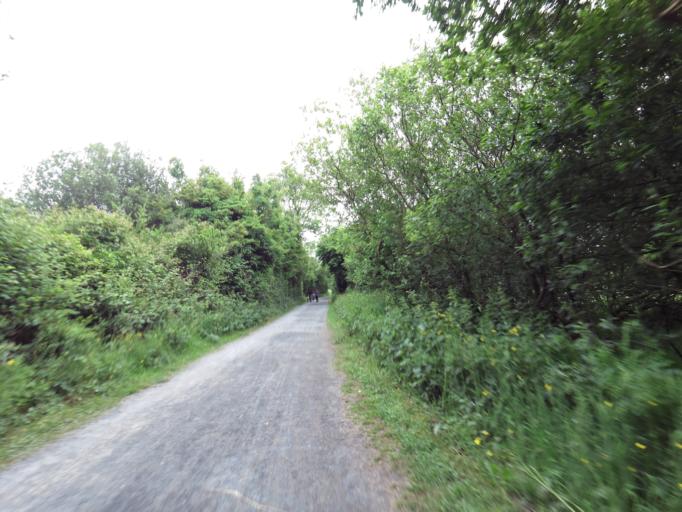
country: IE
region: Connaught
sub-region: County Galway
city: Gaillimh
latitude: 53.2921
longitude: -9.0683
